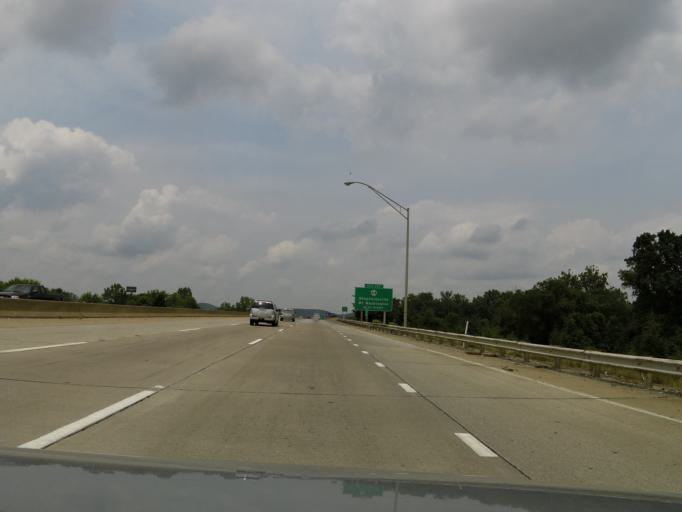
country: US
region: Kentucky
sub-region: Bullitt County
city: Shepherdsville
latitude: 37.9836
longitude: -85.6999
